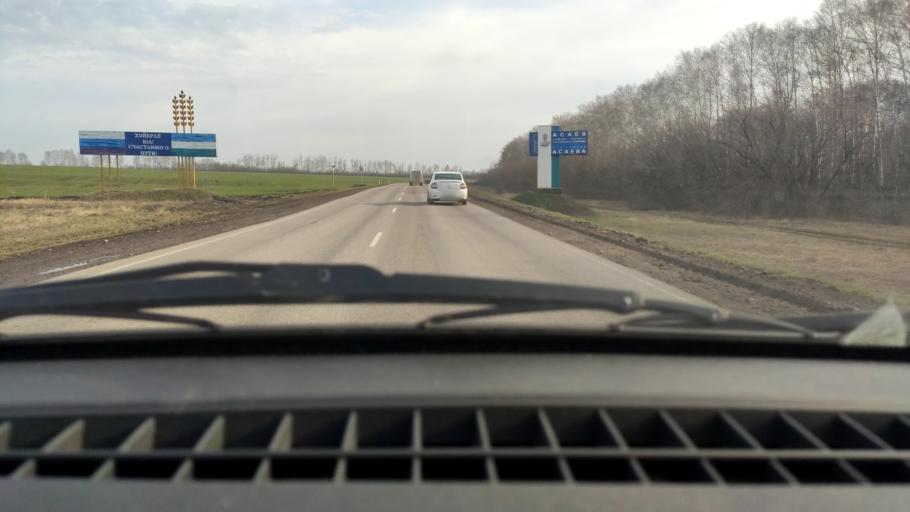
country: RU
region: Bashkortostan
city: Chishmy
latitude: 54.4918
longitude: 55.2762
